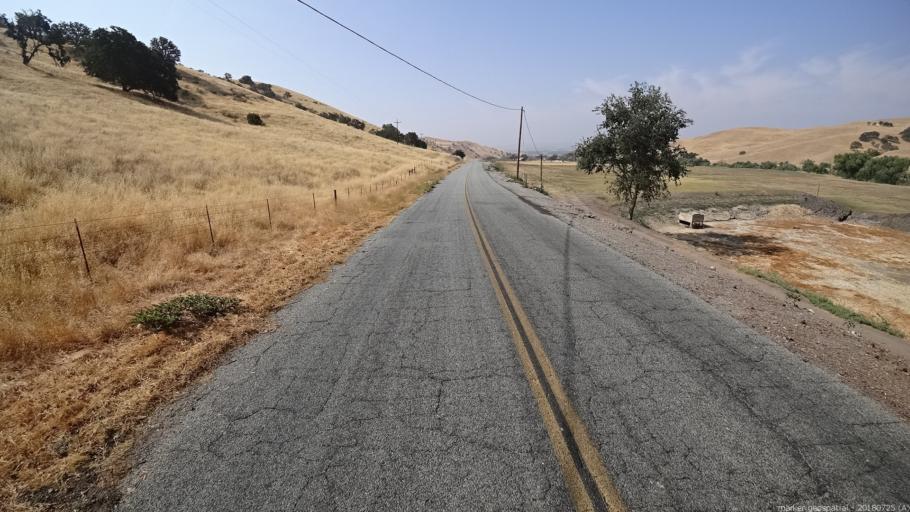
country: US
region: California
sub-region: San Luis Obispo County
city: San Miguel
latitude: 35.8007
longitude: -120.6775
